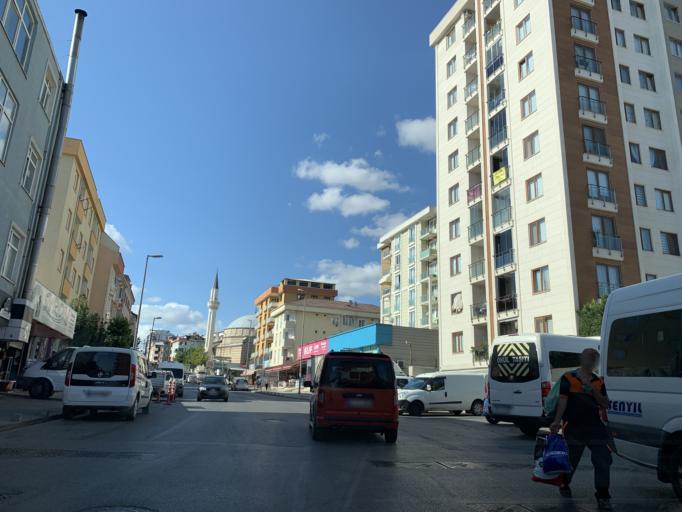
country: TR
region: Istanbul
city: Pendik
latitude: 40.8862
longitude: 29.2730
